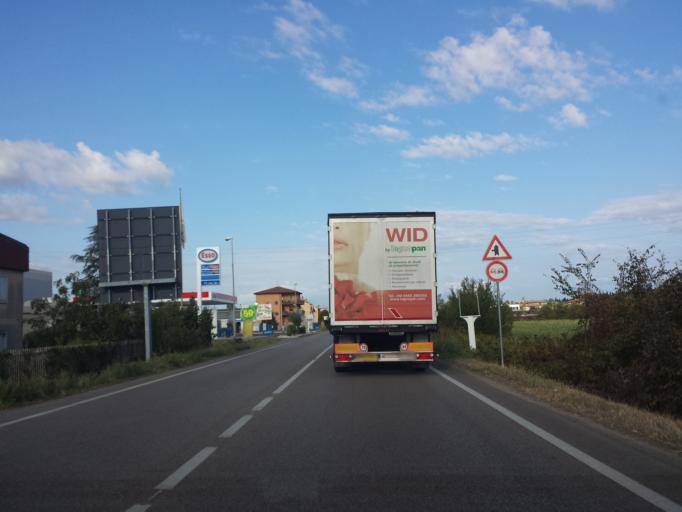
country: IT
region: Veneto
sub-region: Provincia di Verona
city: San Martino Buon Albergo
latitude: 45.4210
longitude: 11.1140
